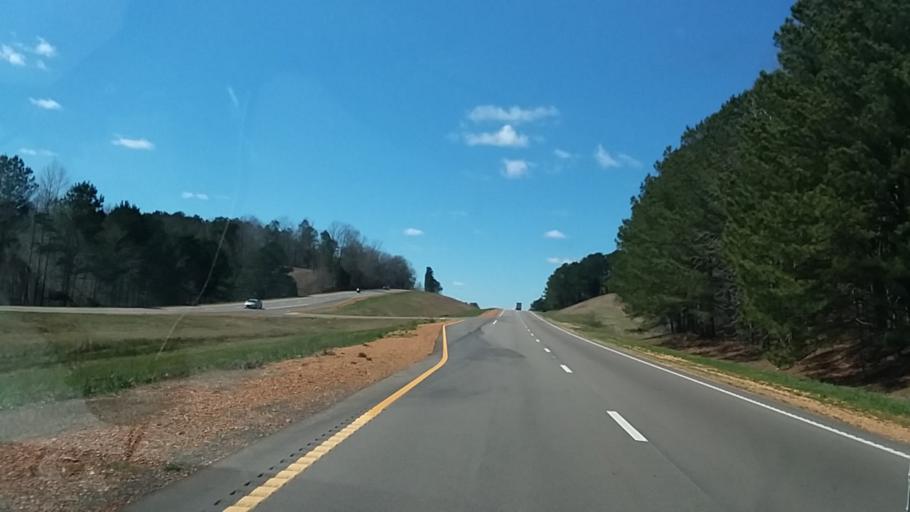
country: US
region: Mississippi
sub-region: Alcorn County
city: Farmington
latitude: 34.8537
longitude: -88.3594
